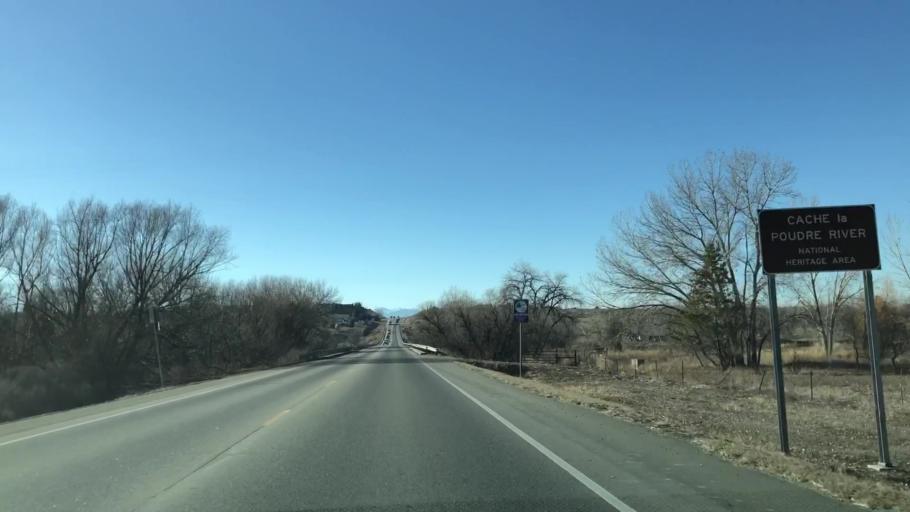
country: US
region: Colorado
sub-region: Weld County
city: Windsor
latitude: 40.4792
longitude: -104.9523
